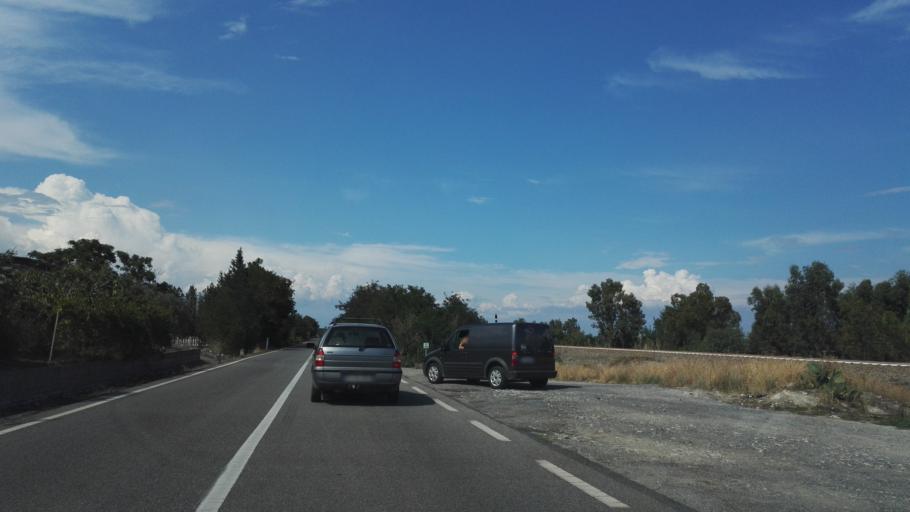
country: IT
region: Calabria
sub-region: Provincia di Catanzaro
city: Badolato Marina
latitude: 38.5531
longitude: 16.5705
